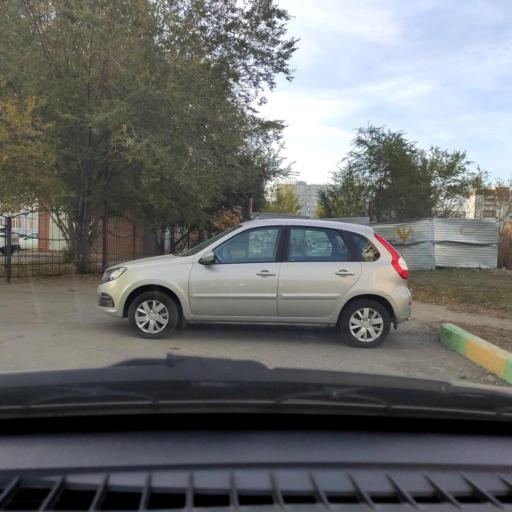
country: RU
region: Samara
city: Tol'yatti
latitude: 53.5436
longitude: 49.3592
